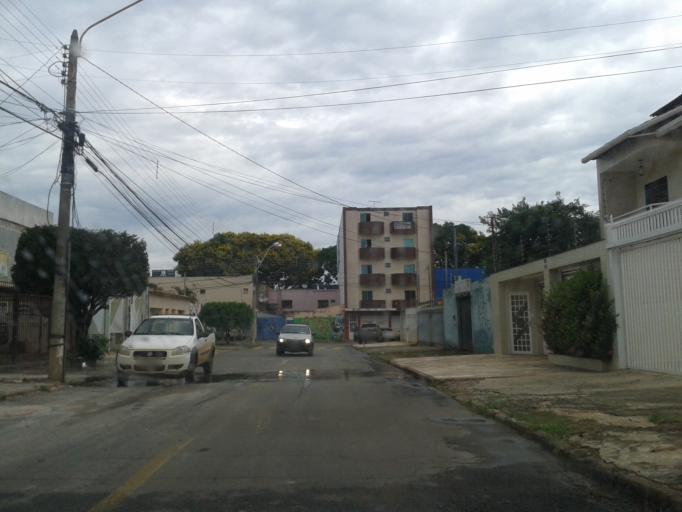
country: BR
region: Federal District
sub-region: Brasilia
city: Brasilia
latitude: -15.8242
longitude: -48.0578
